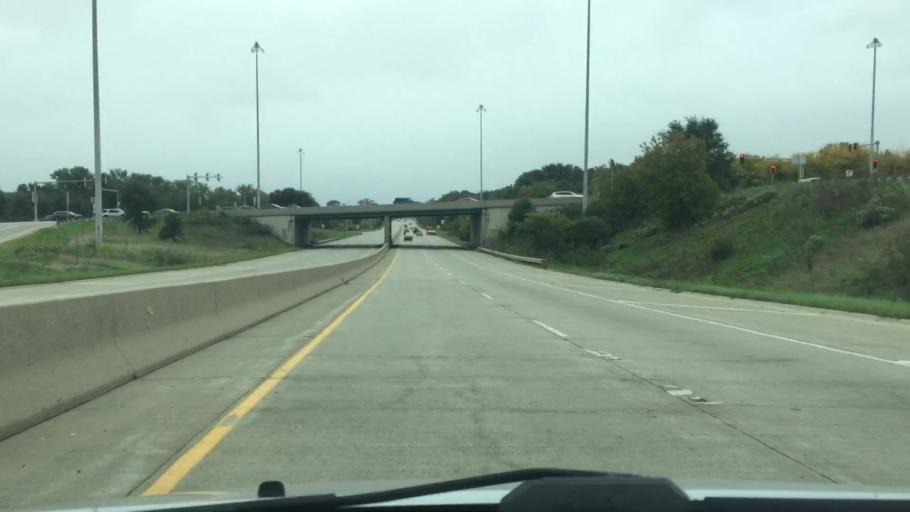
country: US
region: Illinois
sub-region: McHenry County
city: Crystal Lake
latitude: 42.2270
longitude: -88.2876
